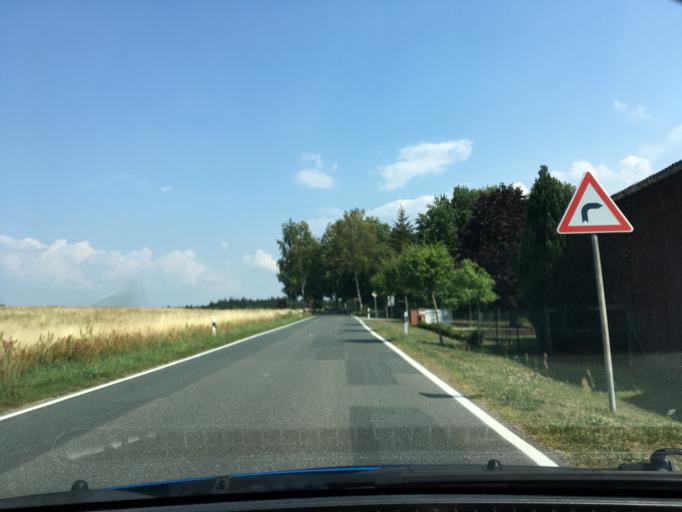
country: DE
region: Lower Saxony
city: Tosterglope
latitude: 53.2411
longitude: 10.7969
